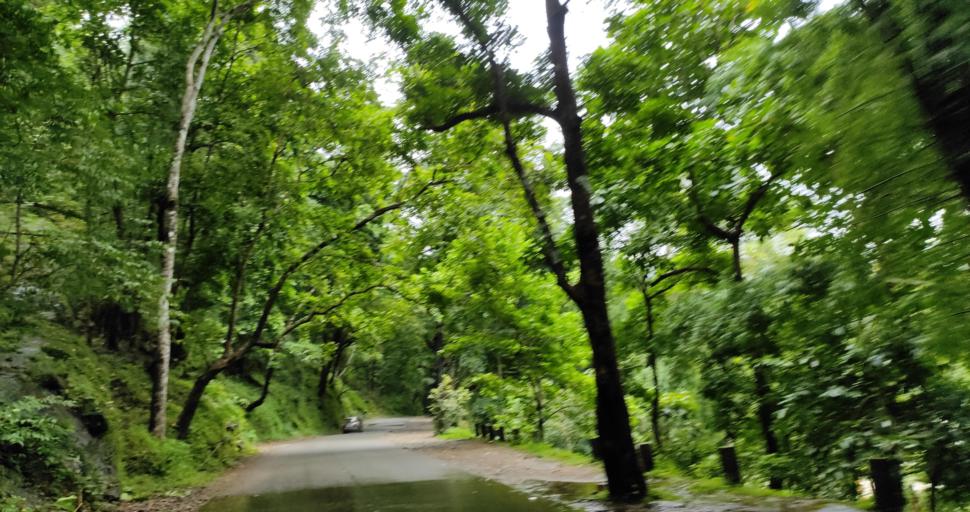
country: IN
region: Kerala
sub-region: Ernakulam
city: Angamali
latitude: 10.2918
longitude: 76.5660
